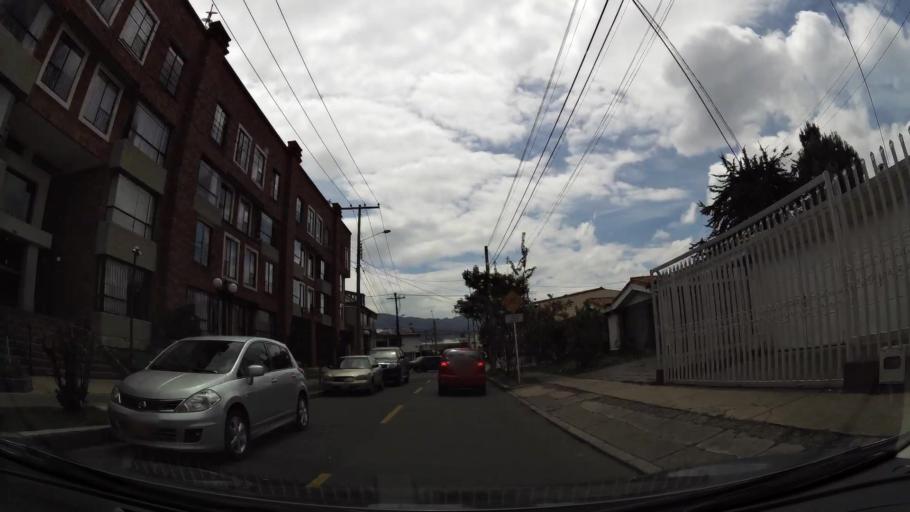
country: CO
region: Bogota D.C.
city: Barrio San Luis
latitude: 4.7020
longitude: -74.0598
